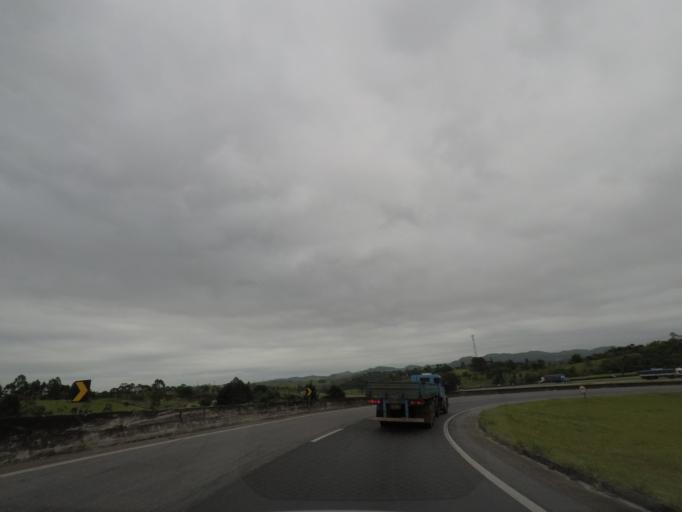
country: BR
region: Sao Paulo
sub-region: Jacarei
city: Jacarei
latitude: -23.3092
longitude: -46.0461
